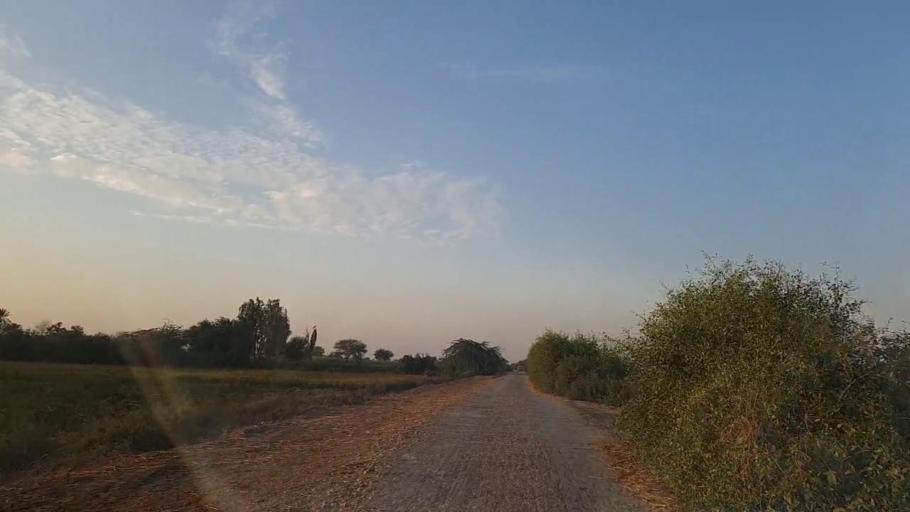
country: PK
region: Sindh
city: Chuhar Jamali
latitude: 24.4525
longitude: 68.1178
